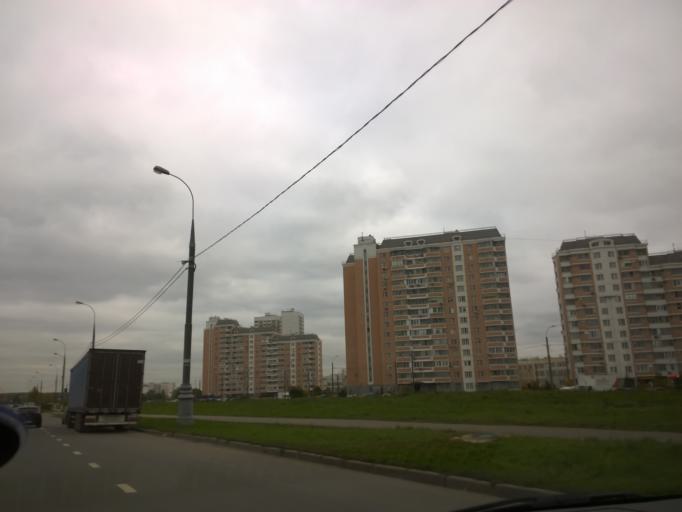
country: RU
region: Moskovskaya
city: Kommunarka
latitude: 55.5322
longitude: 37.4993
